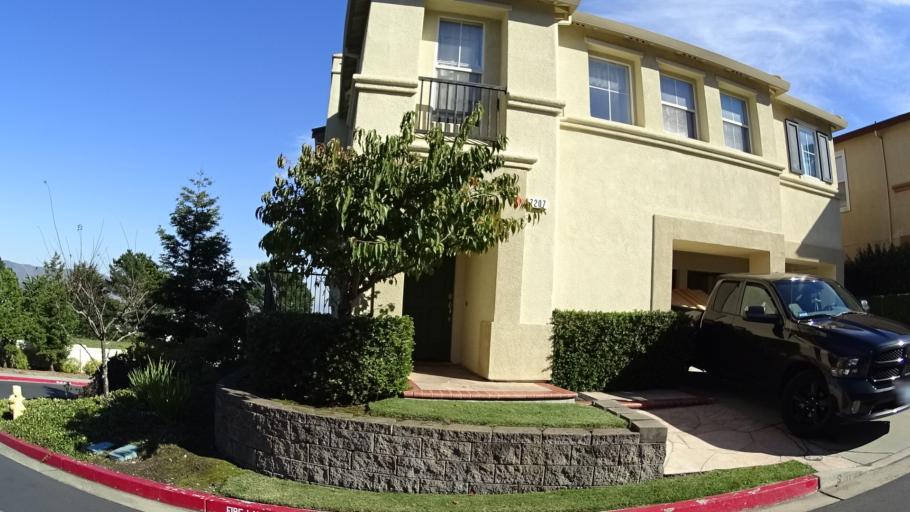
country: US
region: California
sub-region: San Mateo County
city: Pacifica
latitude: 37.6407
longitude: -122.4629
